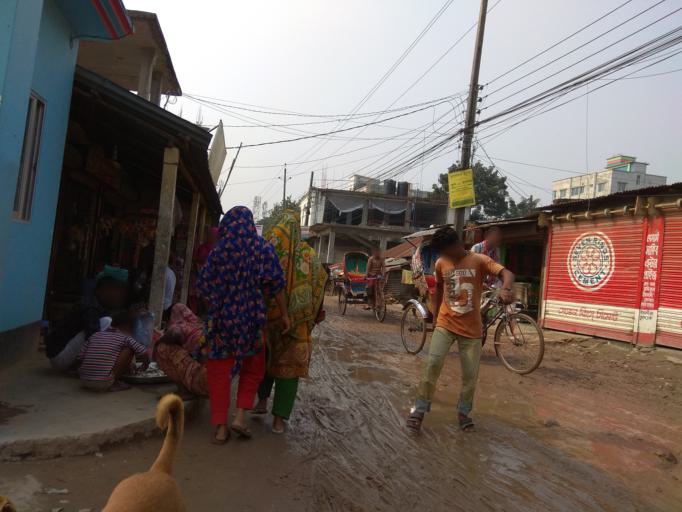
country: BD
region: Dhaka
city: Tungi
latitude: 23.8543
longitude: 90.3847
